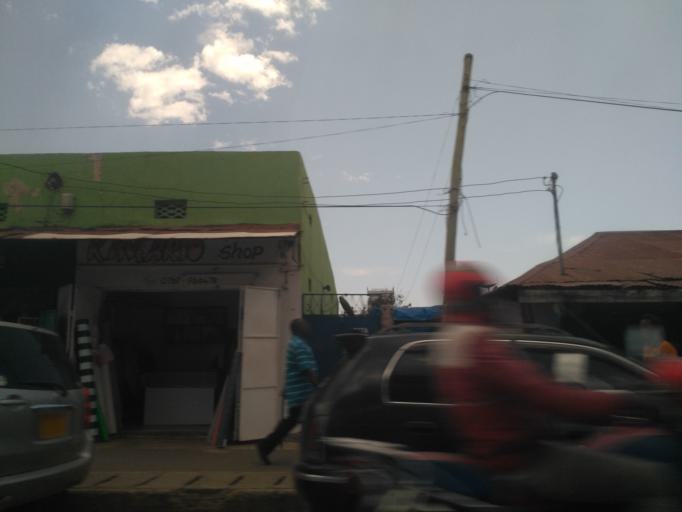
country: TZ
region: Mwanza
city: Mwanza
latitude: -2.5176
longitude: 32.9051
